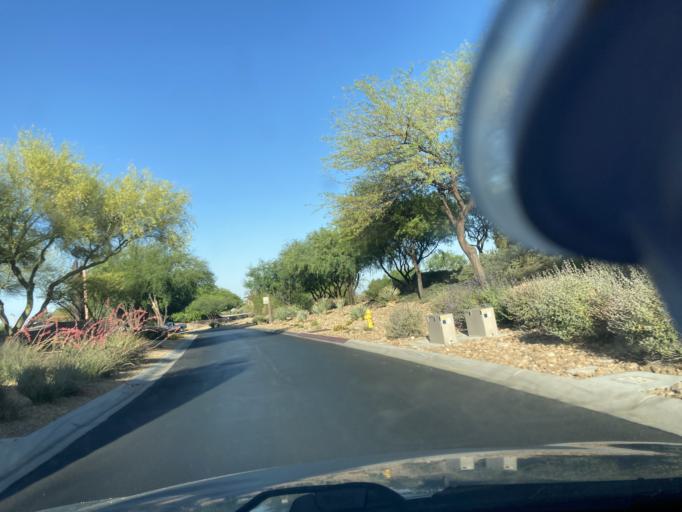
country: US
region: Nevada
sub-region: Clark County
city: Summerlin South
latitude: 36.1257
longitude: -115.3416
